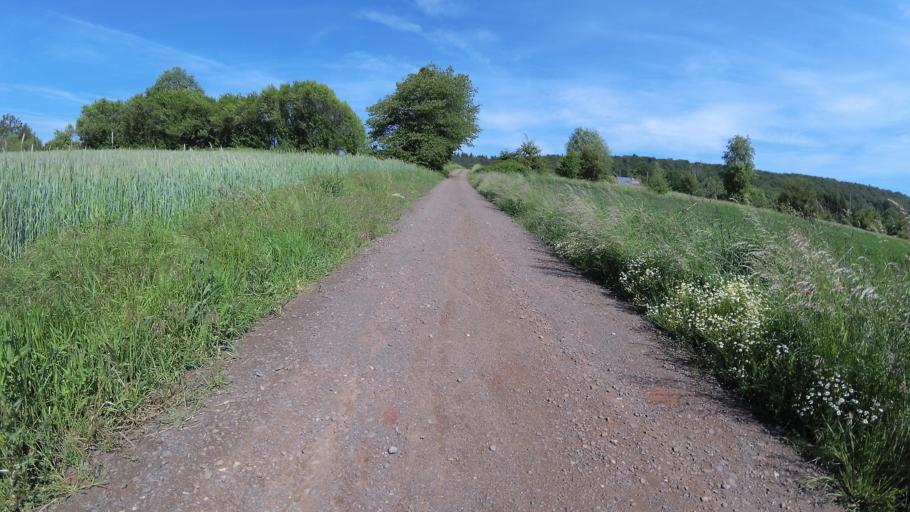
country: DE
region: Saarland
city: Ottweiler
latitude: 49.4331
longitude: 7.1713
